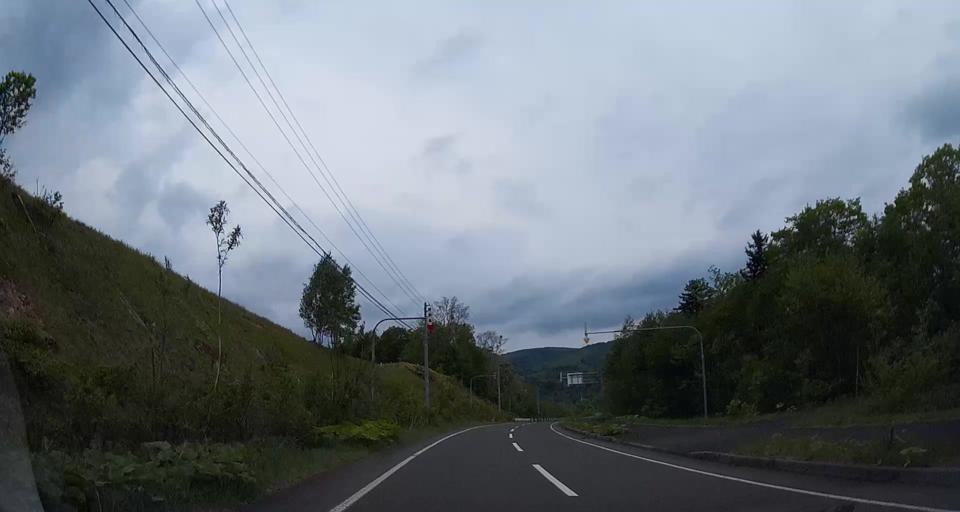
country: JP
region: Hokkaido
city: Shiraoi
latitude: 42.6733
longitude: 141.1040
